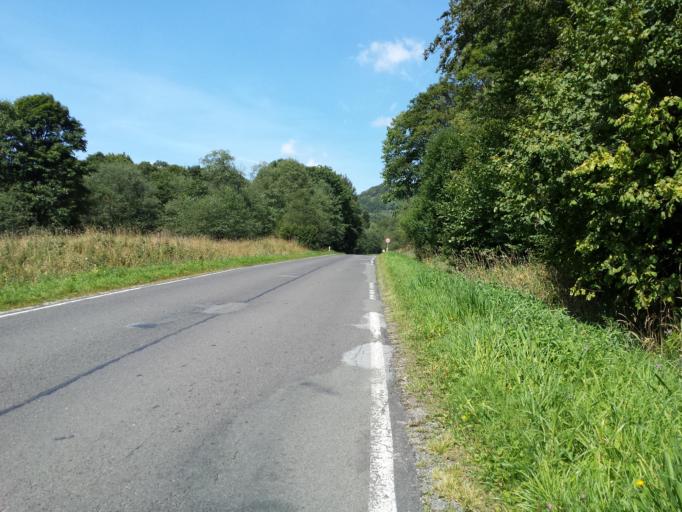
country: PL
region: Subcarpathian Voivodeship
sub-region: Powiat bieszczadzki
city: Lutowiska
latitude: 49.1140
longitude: 22.6118
